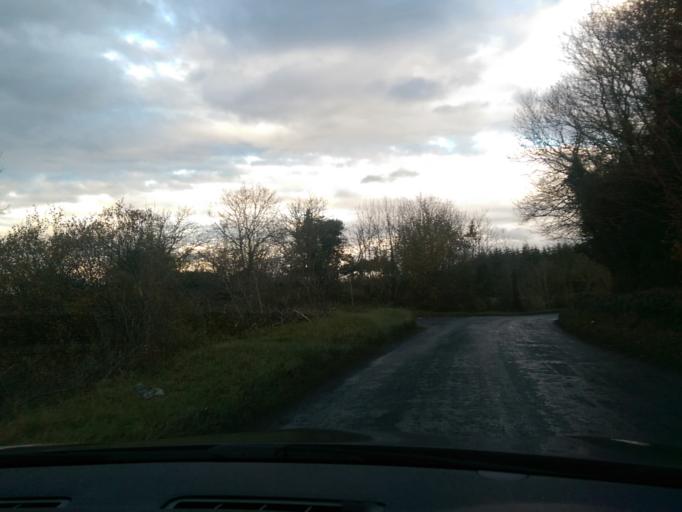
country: IE
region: Connaught
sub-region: County Galway
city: Athenry
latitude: 53.4651
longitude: -8.5393
